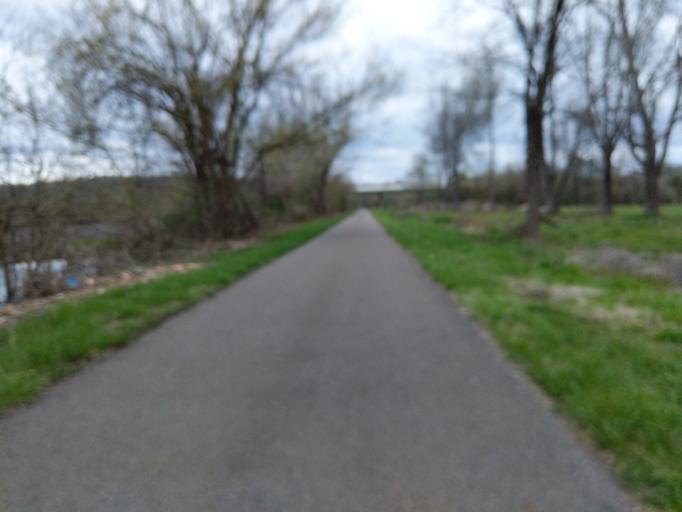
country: US
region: Ohio
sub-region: Athens County
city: The Plains
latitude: 39.3684
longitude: -82.1155
